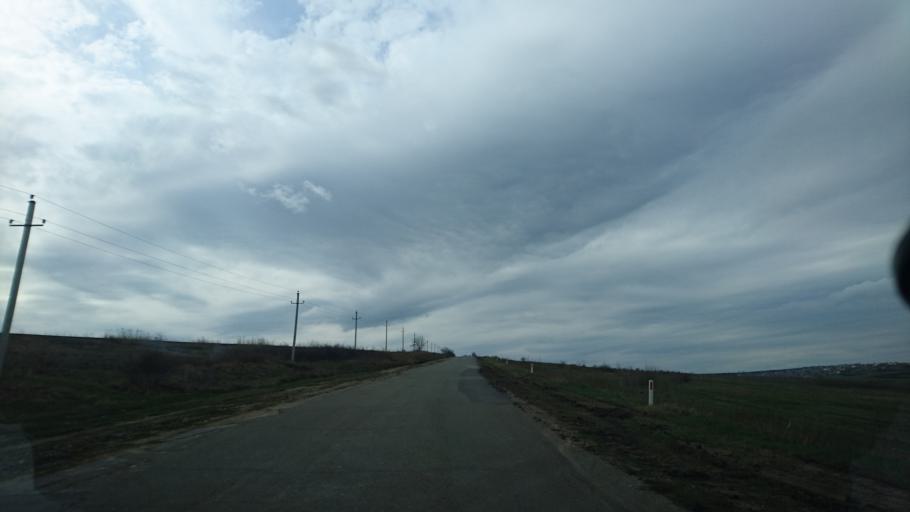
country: MD
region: Cantemir
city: Visniovca
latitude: 46.3355
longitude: 28.4390
